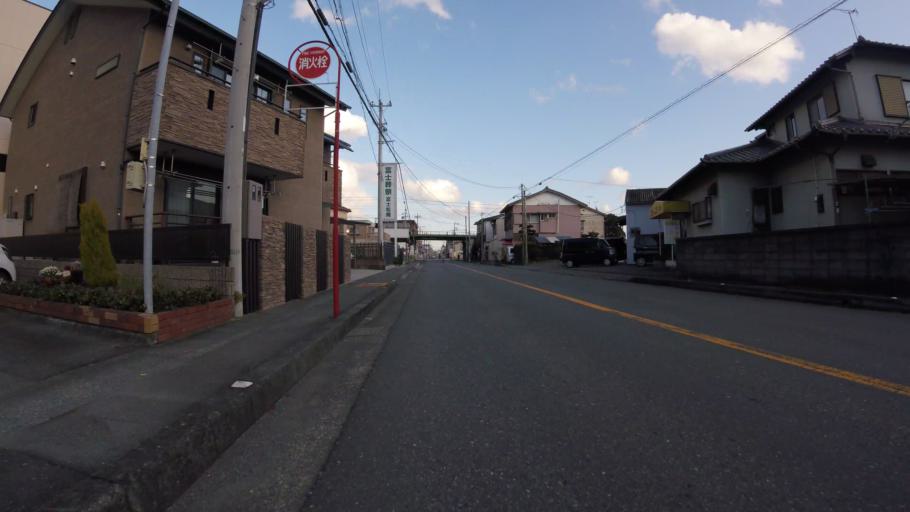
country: JP
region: Shizuoka
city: Fuji
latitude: 35.1557
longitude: 138.6383
